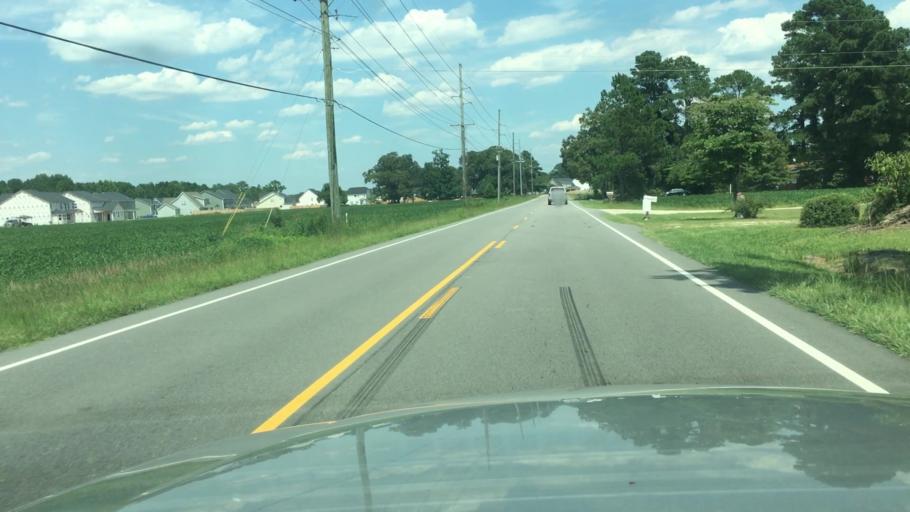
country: US
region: North Carolina
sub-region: Cumberland County
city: Hope Mills
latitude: 34.9484
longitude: -78.8623
